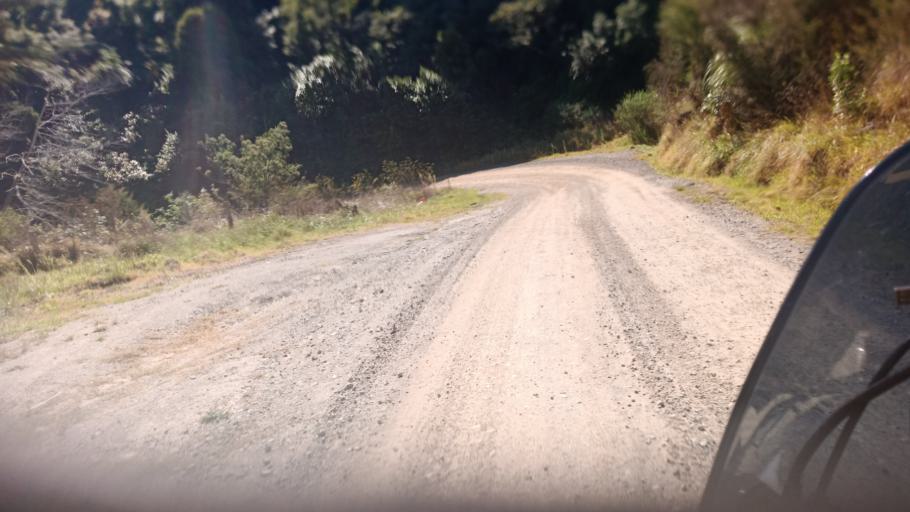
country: NZ
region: Gisborne
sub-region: Gisborne District
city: Gisborne
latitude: -38.3932
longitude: 177.6684
